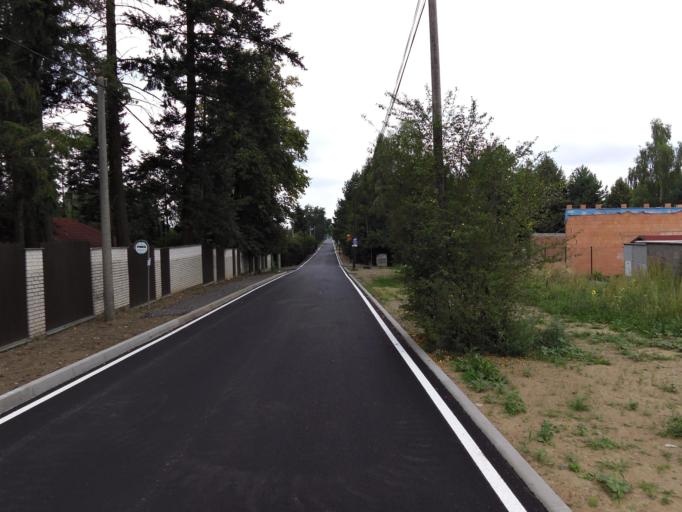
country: CZ
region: Central Bohemia
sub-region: Okres Benesov
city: Pysely
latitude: 49.8727
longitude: 14.6950
